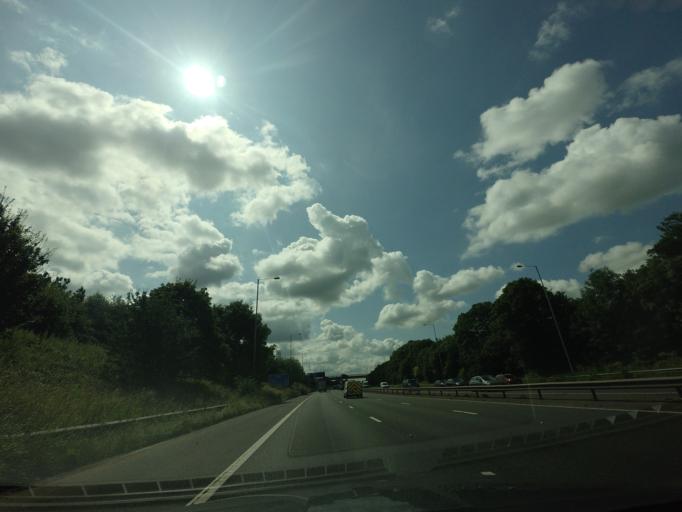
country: GB
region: England
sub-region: Lancashire
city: Clayton-le-Woods
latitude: 53.6893
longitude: -2.6778
